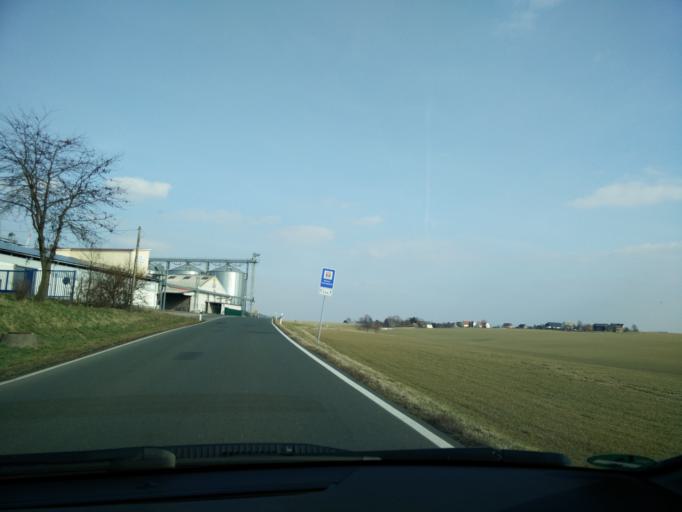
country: DE
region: Saxony
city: Zettlitz
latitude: 51.0789
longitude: 12.8564
